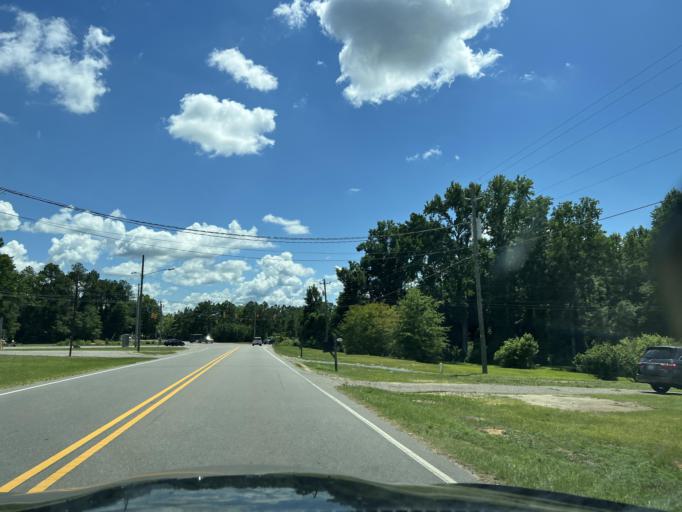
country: US
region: North Carolina
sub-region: Lee County
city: Sanford
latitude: 35.4461
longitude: -79.1726
